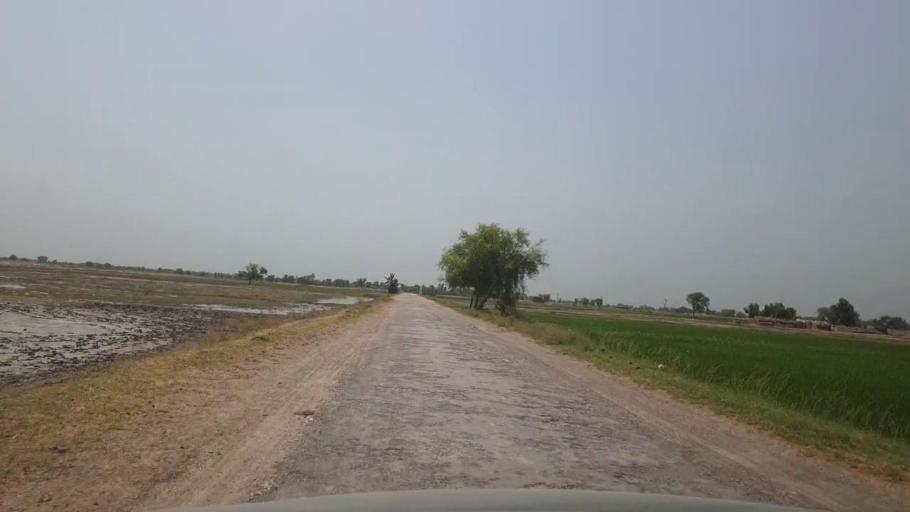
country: PK
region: Sindh
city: Garhi Yasin
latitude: 27.9153
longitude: 68.4039
